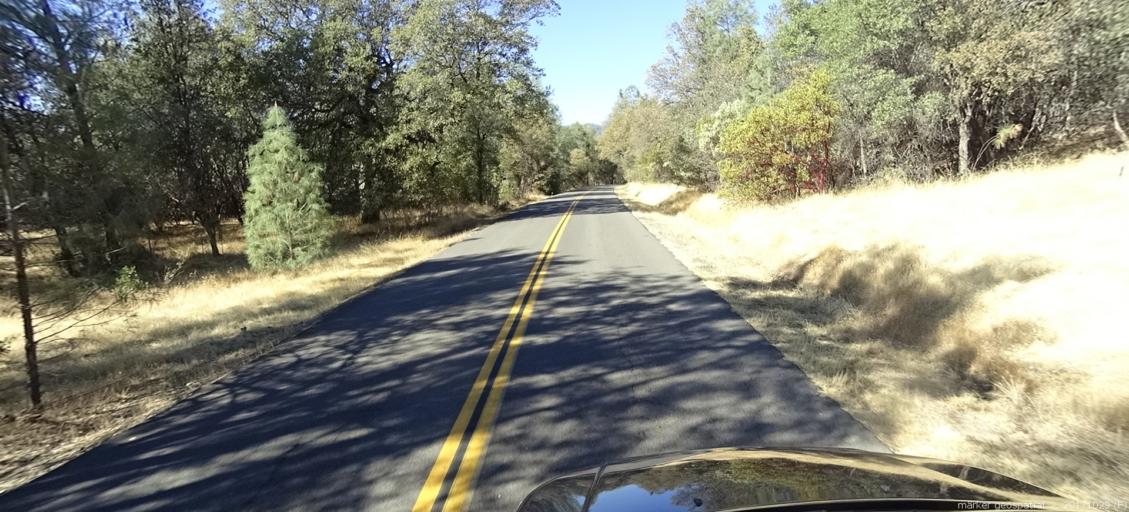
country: US
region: California
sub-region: Shasta County
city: Shasta
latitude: 40.4784
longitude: -122.6491
